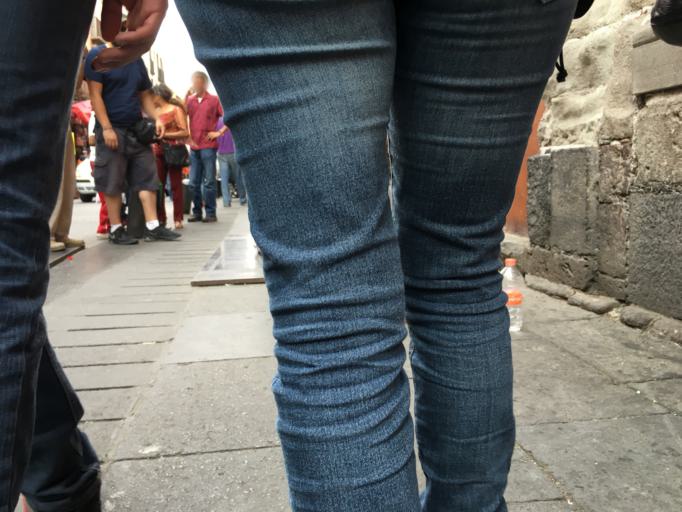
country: MX
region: Mexico City
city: Mexico City
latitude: 19.4333
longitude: -99.1287
